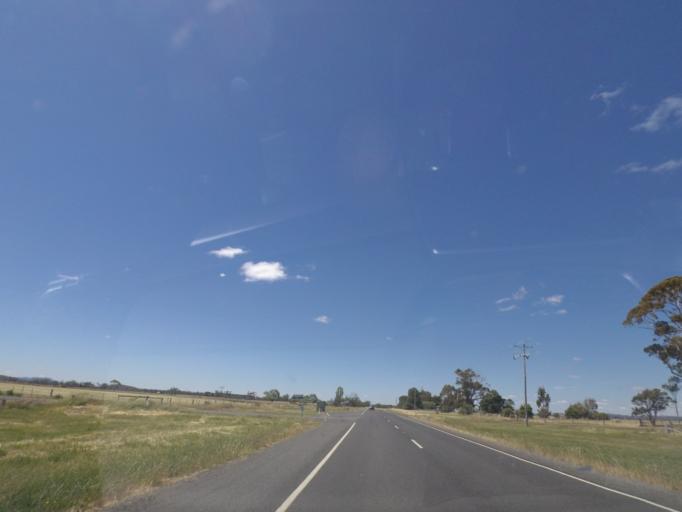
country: AU
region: Victoria
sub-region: Mount Alexander
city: Castlemaine
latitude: -37.2270
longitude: 144.3366
